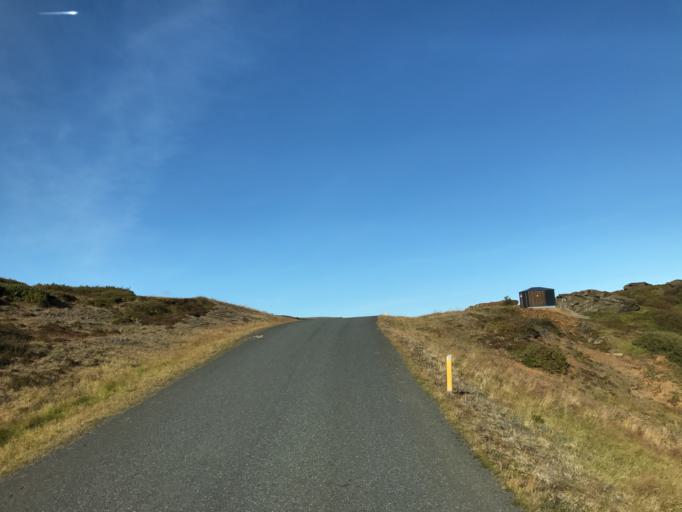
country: IS
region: South
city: Hveragerdi
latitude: 64.1451
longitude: -21.2603
